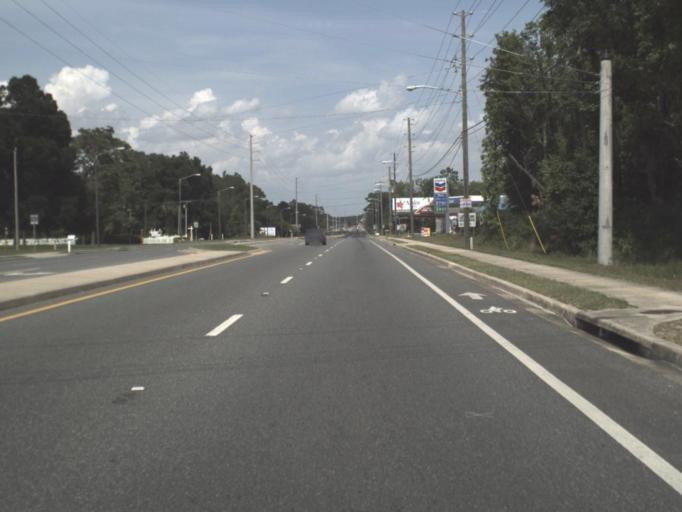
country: US
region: Florida
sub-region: Putnam County
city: Palatka
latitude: 29.6357
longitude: -81.7056
